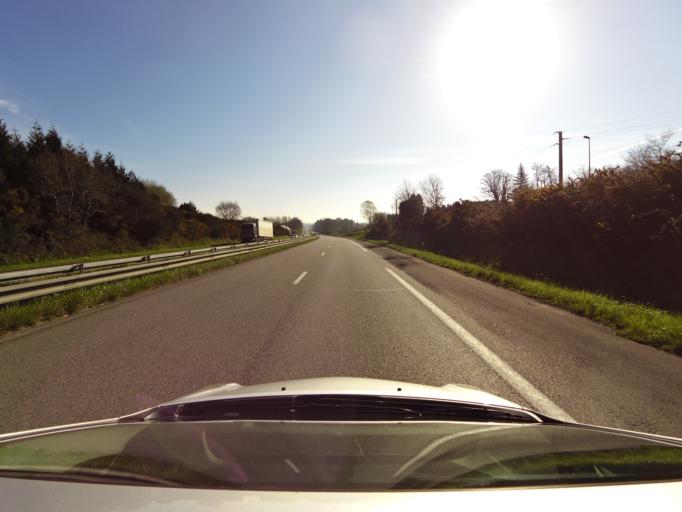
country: FR
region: Brittany
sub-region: Departement du Morbihan
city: Languidic
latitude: 47.8332
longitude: -3.1815
